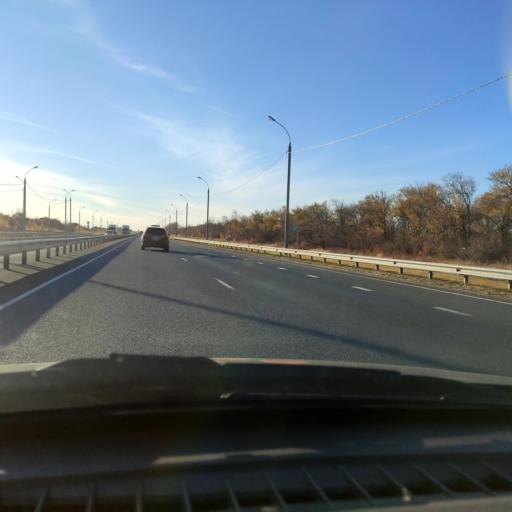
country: RU
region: Samara
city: Varlamovo
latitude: 53.1959
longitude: 48.2900
